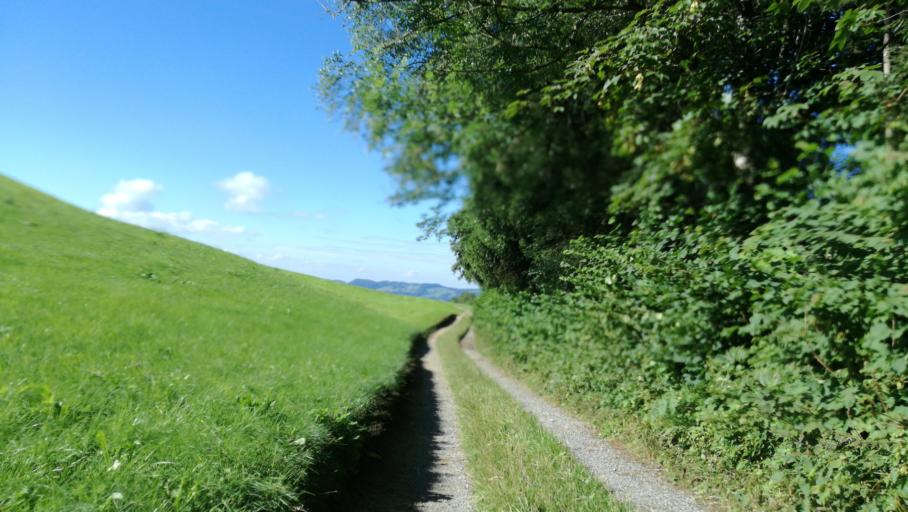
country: CH
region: Zug
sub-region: Zug
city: Unterageri
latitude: 47.1574
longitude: 8.5553
